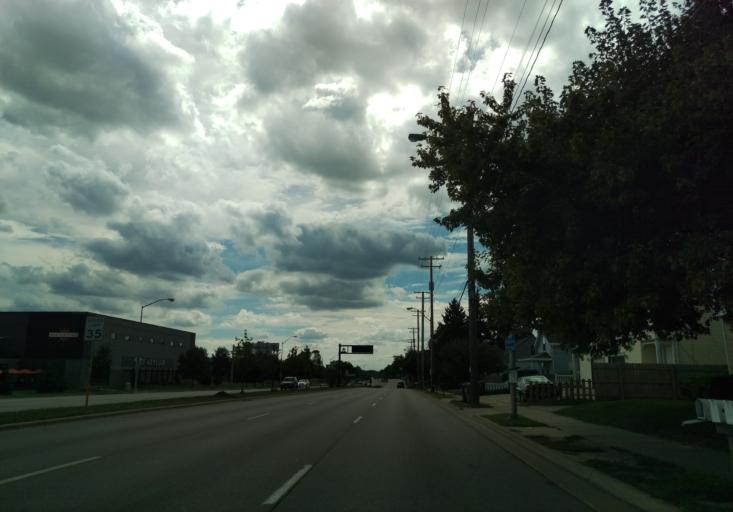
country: US
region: Wisconsin
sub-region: Dane County
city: Maple Bluff
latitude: 43.1214
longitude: -89.3551
